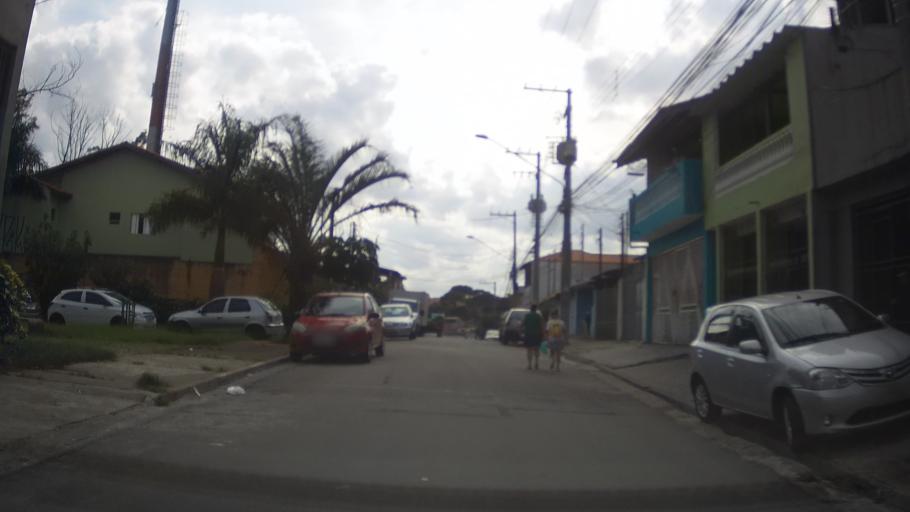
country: BR
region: Sao Paulo
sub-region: Guarulhos
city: Guarulhos
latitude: -23.4576
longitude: -46.5031
